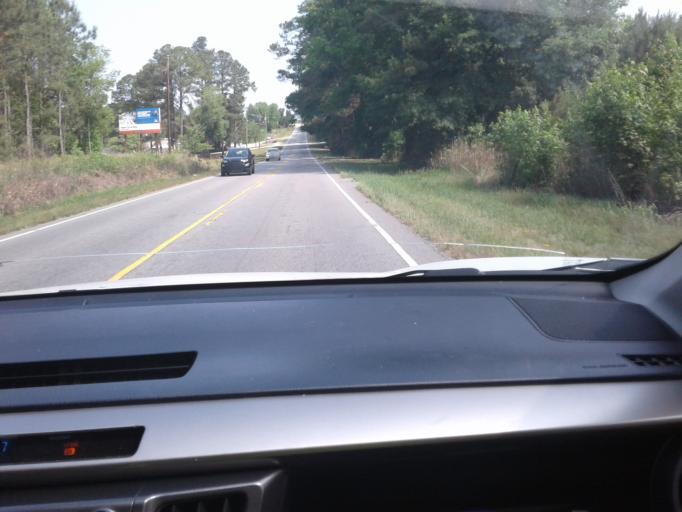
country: US
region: North Carolina
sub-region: Harnett County
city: Coats
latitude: 35.4382
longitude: -78.6815
